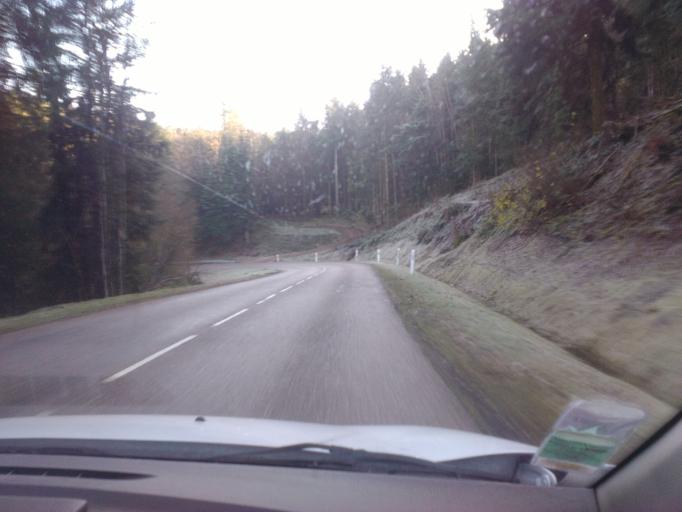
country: FR
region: Lorraine
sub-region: Departement des Vosges
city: Remiremont
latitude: 47.9824
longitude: 6.5580
